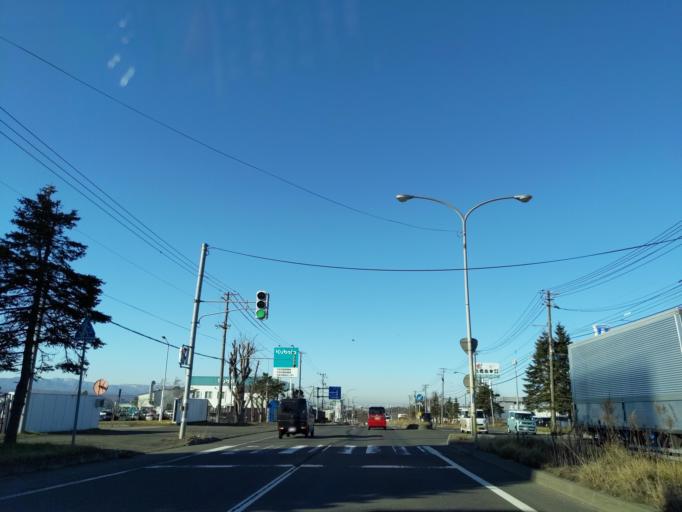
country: JP
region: Hokkaido
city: Kitahiroshima
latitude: 42.9622
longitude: 141.4903
